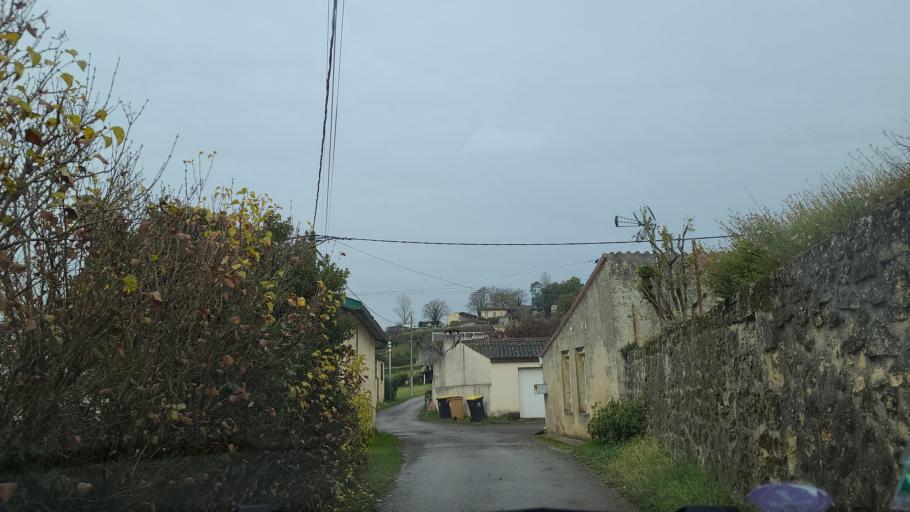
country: FR
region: Aquitaine
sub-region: Departement de la Gironde
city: Bourg
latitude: 45.0426
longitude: -0.5748
